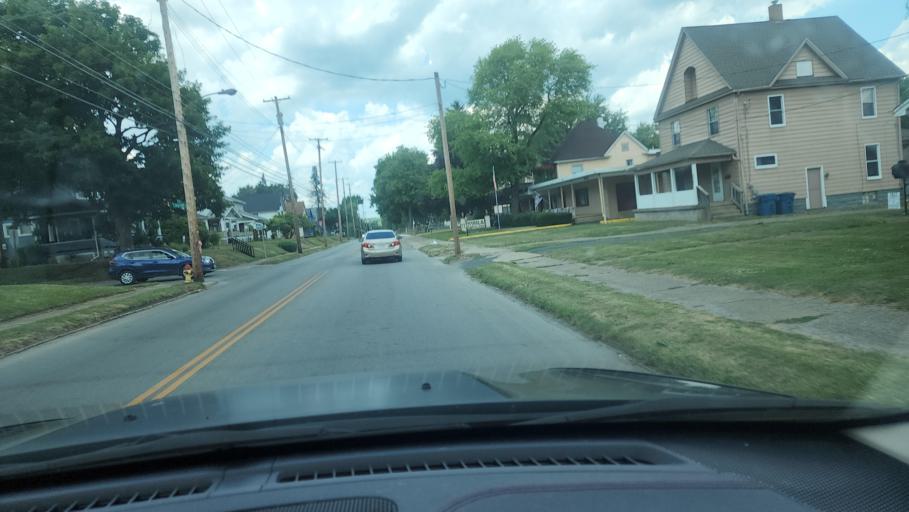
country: US
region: Ohio
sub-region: Mahoning County
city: Struthers
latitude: 41.0495
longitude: -80.5917
